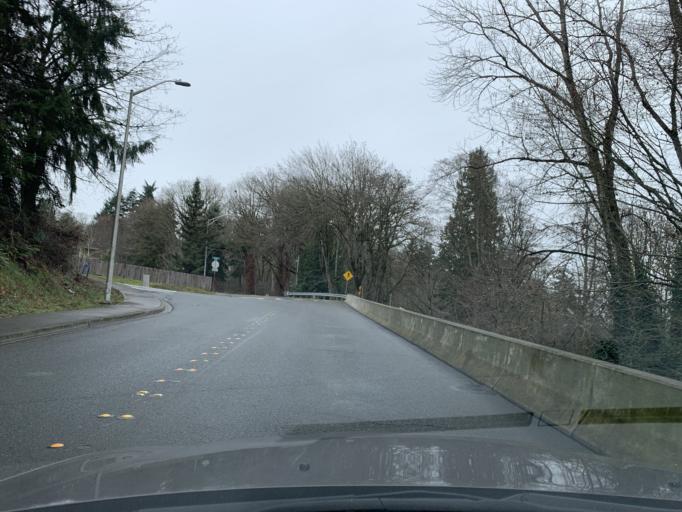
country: US
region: Washington
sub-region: King County
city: Tukwila
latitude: 47.4593
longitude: -122.2699
